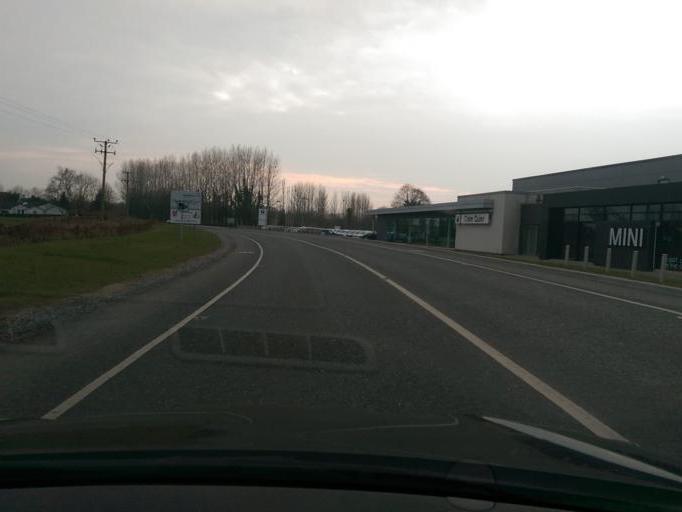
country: IE
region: Leinster
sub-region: An Iarmhi
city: Athlone
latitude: 53.4391
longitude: -7.8981
